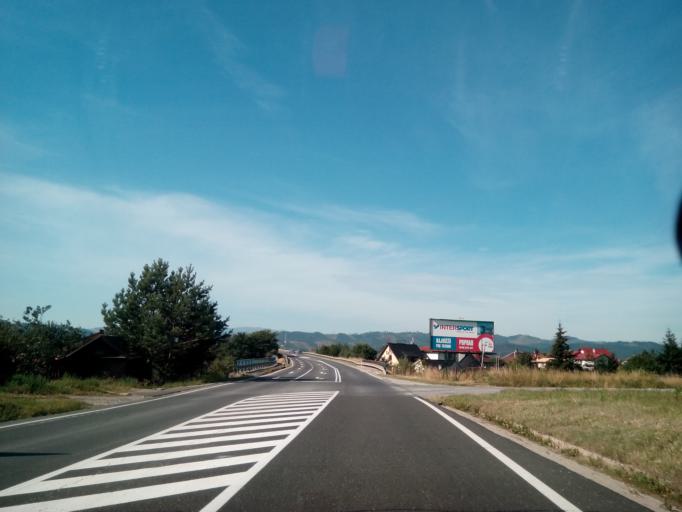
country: SK
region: Presovsky
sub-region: Okres Poprad
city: Poprad
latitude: 49.0681
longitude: 20.2712
